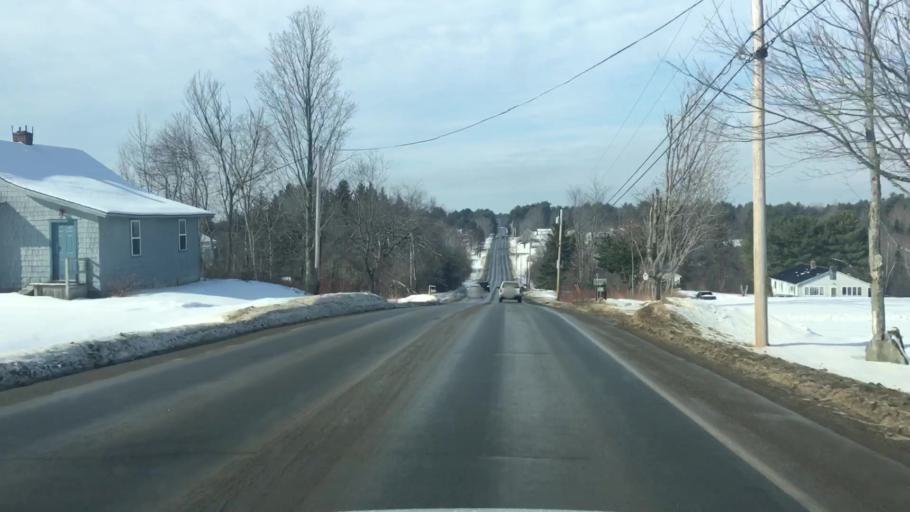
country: US
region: Maine
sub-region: Penobscot County
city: Hermon
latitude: 44.8491
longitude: -68.8762
